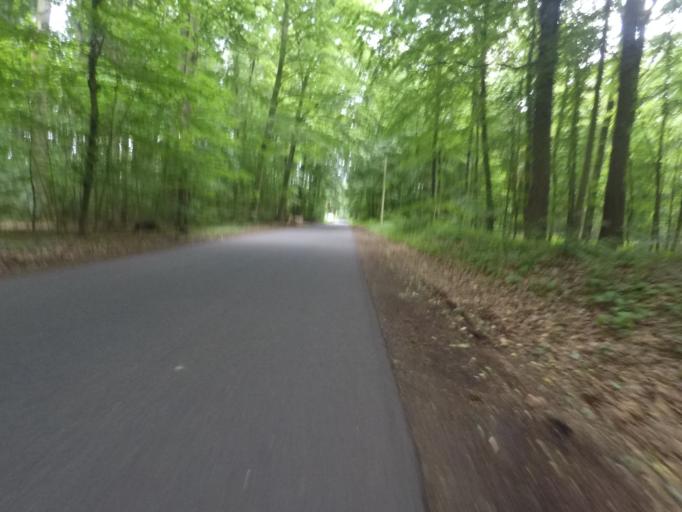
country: DE
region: North Rhine-Westphalia
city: Spenge
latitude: 52.1487
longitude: 8.4750
